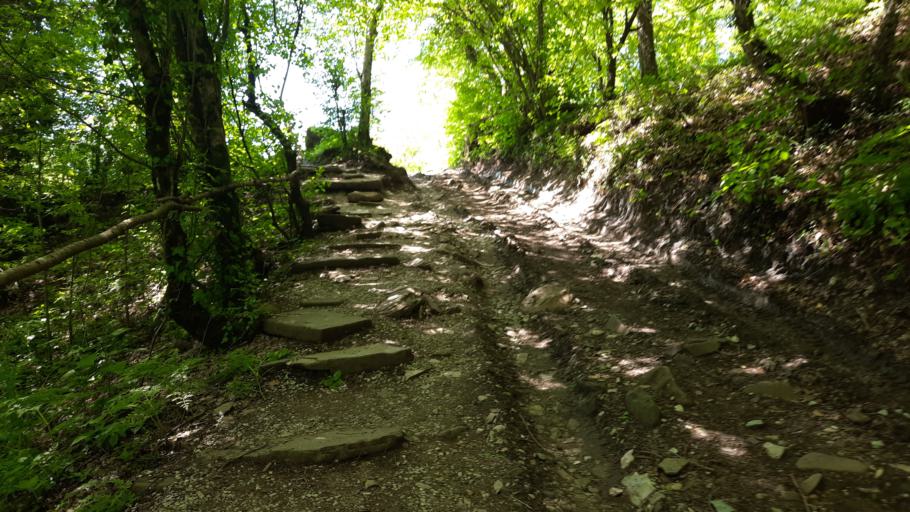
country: RU
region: Krasnodarskiy
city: Divnomorskoye
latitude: 44.5625
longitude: 38.2586
